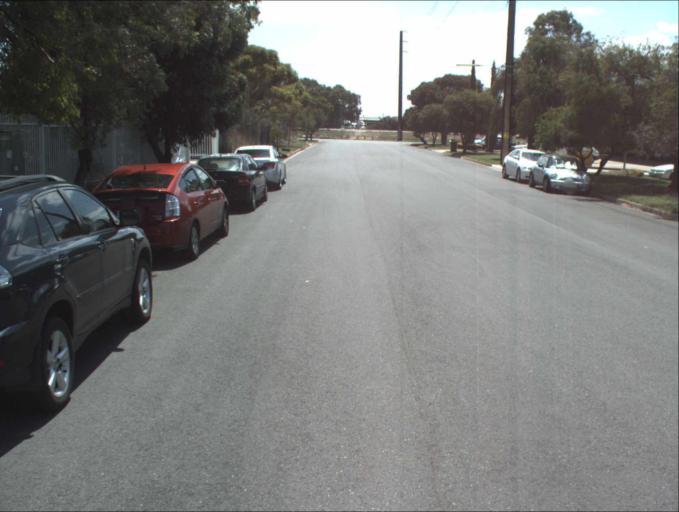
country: AU
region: South Australia
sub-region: Port Adelaide Enfield
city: Blair Athol
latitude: -34.8514
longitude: 138.5697
